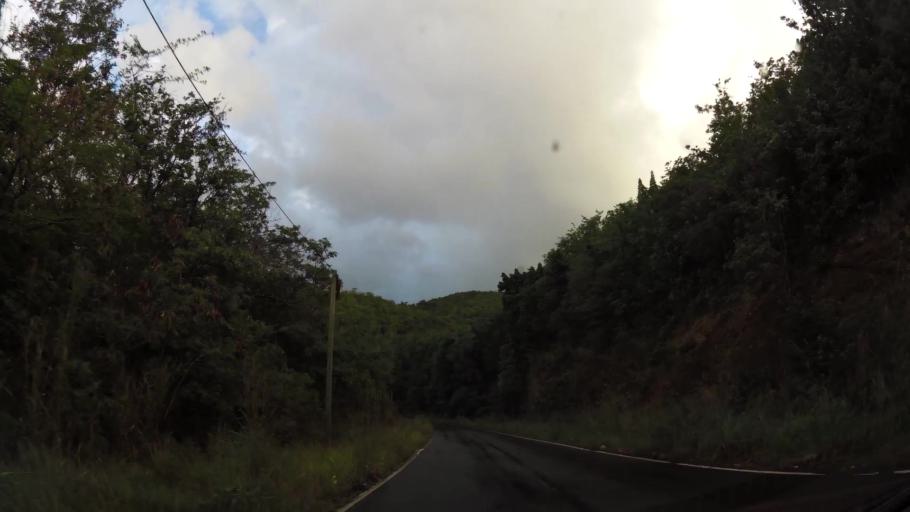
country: DM
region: Saint Peter
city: Colihaut
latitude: 15.5288
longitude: -61.4673
